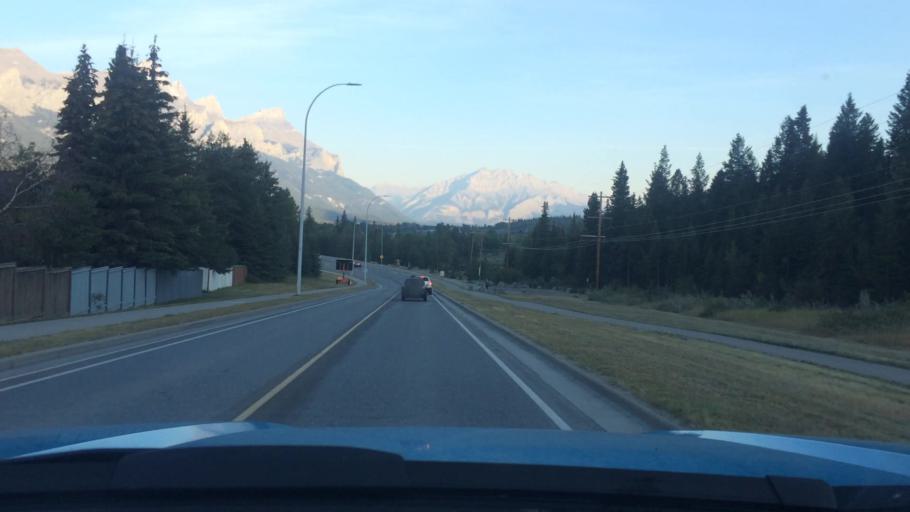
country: CA
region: Alberta
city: Canmore
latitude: 51.0895
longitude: -115.3383
